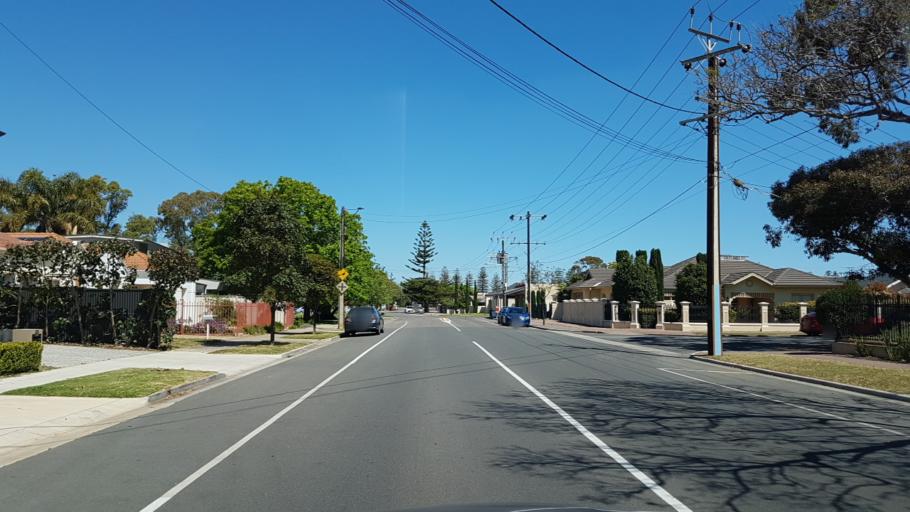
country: AU
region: South Australia
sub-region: Holdfast Bay
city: Glenelg East
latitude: -34.9732
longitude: 138.5286
